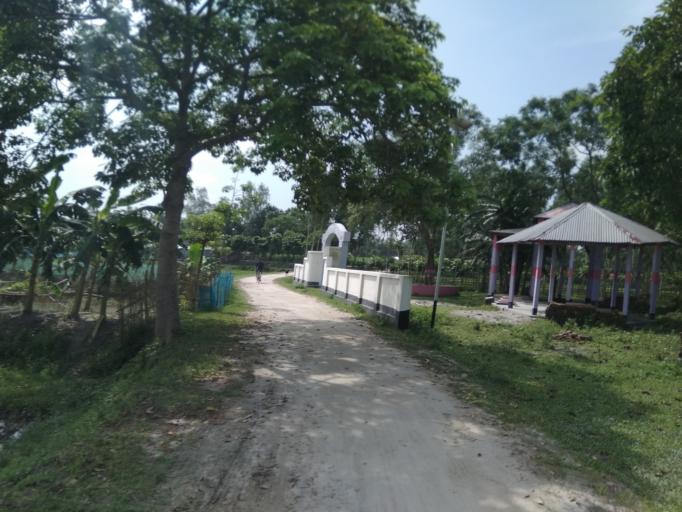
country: BD
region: Rangpur Division
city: Rangpur
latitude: 25.8383
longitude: 89.2040
